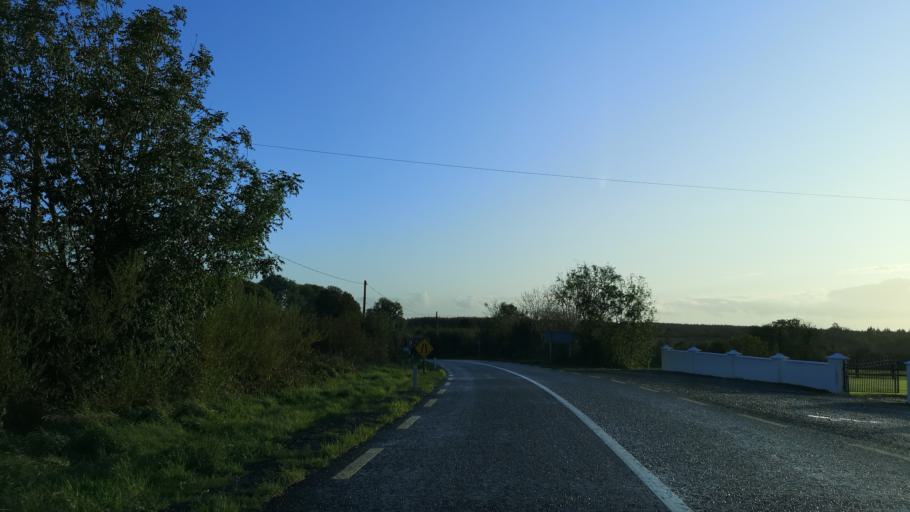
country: IE
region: Connaught
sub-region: Roscommon
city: Castlerea
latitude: 53.7174
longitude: -8.5622
